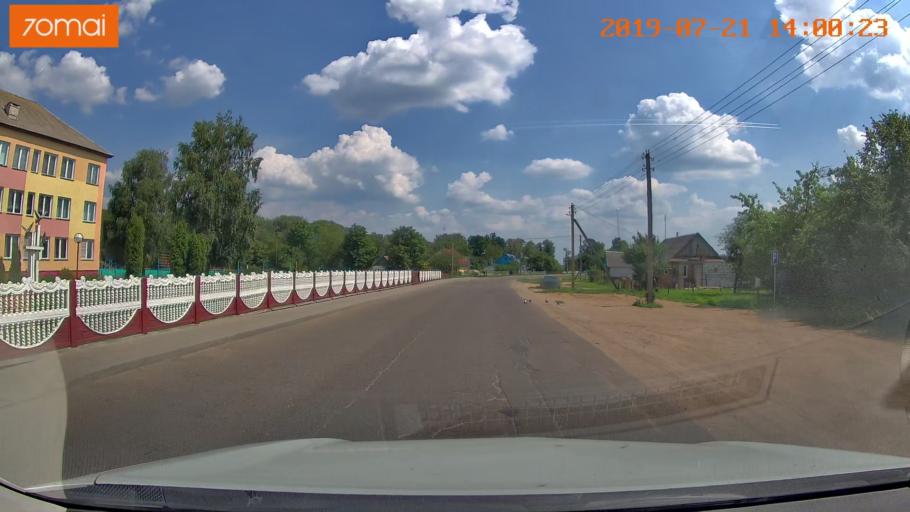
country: BY
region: Grodnenskaya
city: Lyubcha
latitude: 53.7505
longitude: 26.0641
